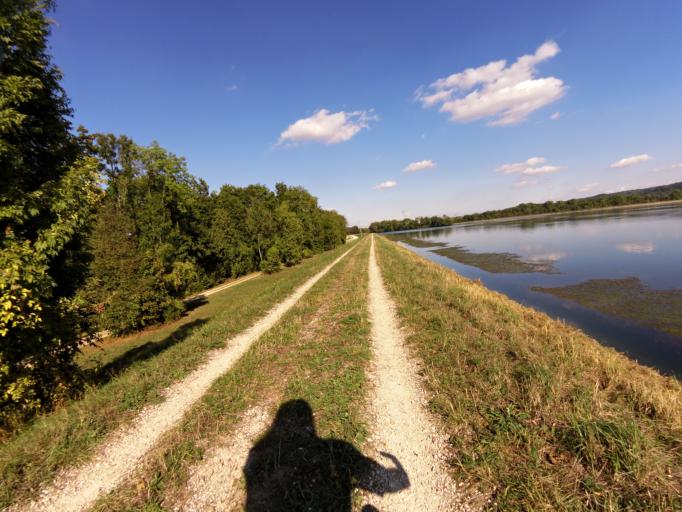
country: DE
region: Bavaria
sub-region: Lower Bavaria
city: Stallwang
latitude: 48.5793
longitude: 12.2083
